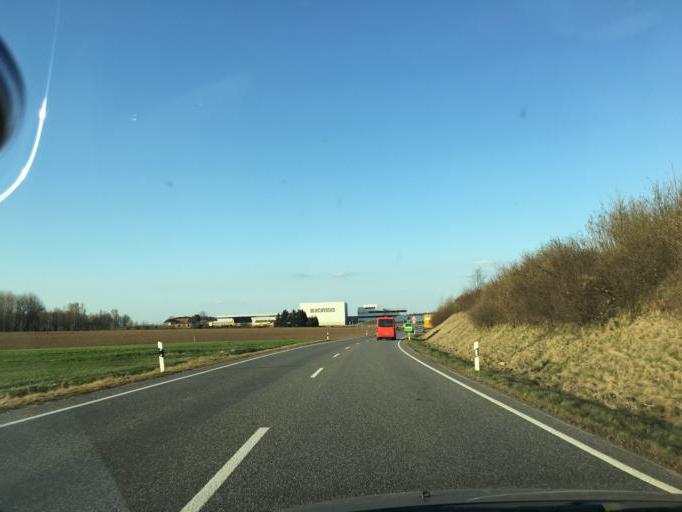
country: DE
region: Saxony
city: Hartmannsdorf
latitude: 50.8886
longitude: 12.7845
